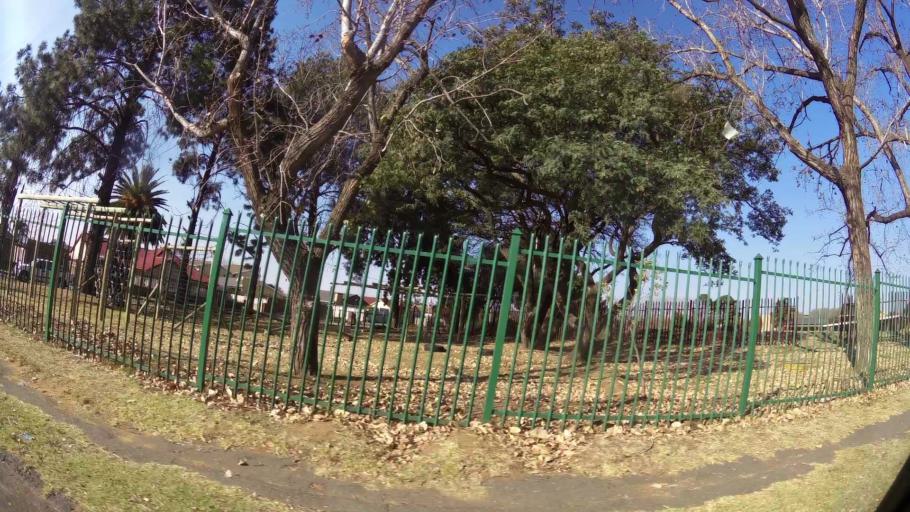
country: ZA
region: Gauteng
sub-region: City of Johannesburg Metropolitan Municipality
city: Johannesburg
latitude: -26.2481
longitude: 28.0092
